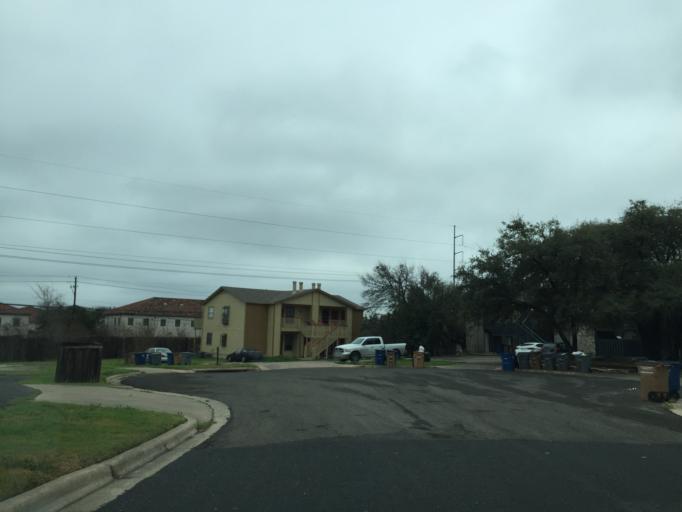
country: US
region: Texas
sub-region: Williamson County
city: Jollyville
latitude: 30.4126
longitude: -97.7301
